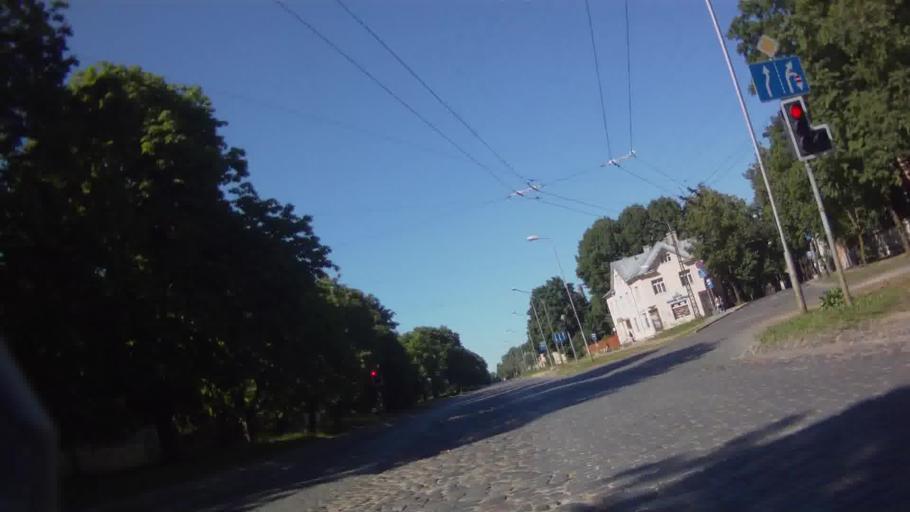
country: LV
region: Riga
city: Riga
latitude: 56.9232
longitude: 24.0898
